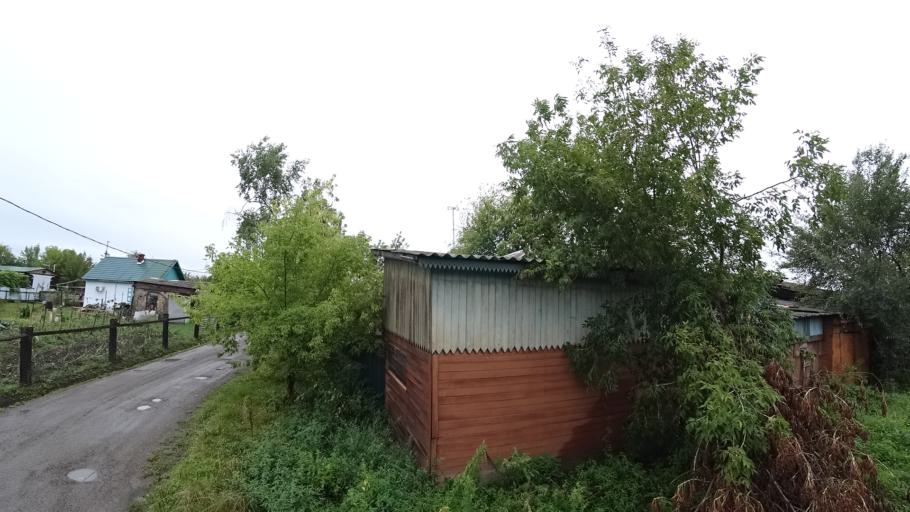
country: RU
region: Primorskiy
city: Monastyrishche
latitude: 44.2030
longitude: 132.4255
